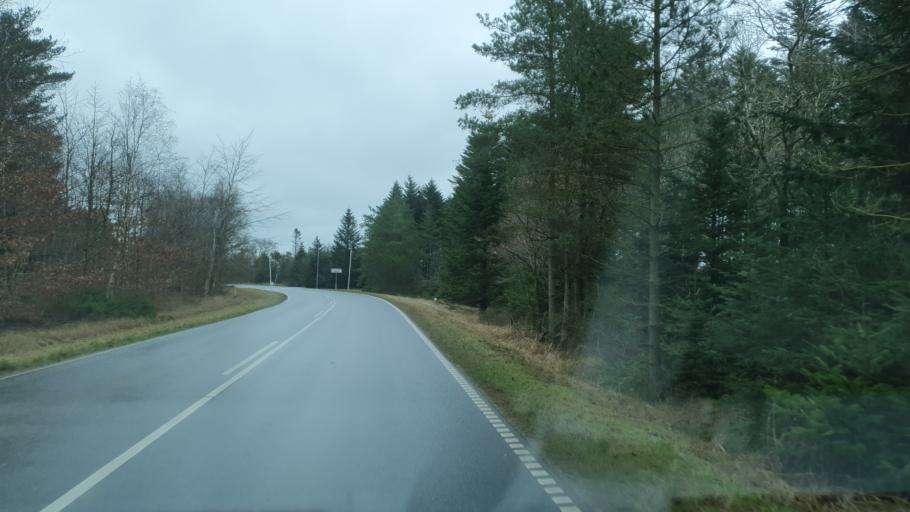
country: DK
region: North Denmark
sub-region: Jammerbugt Kommune
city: Fjerritslev
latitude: 57.1293
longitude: 9.1329
